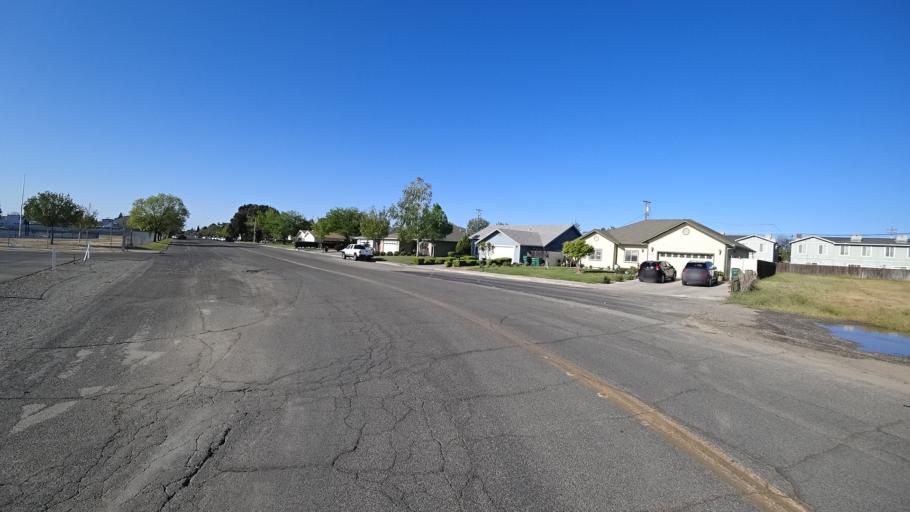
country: US
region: California
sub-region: Glenn County
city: Orland
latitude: 39.7542
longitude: -122.1926
